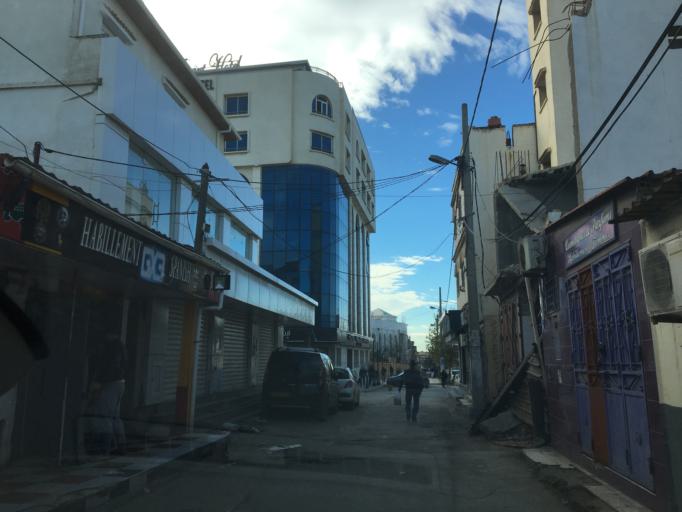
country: DZ
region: Alger
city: Bordj el Kiffan
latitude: 36.7461
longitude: 3.1876
